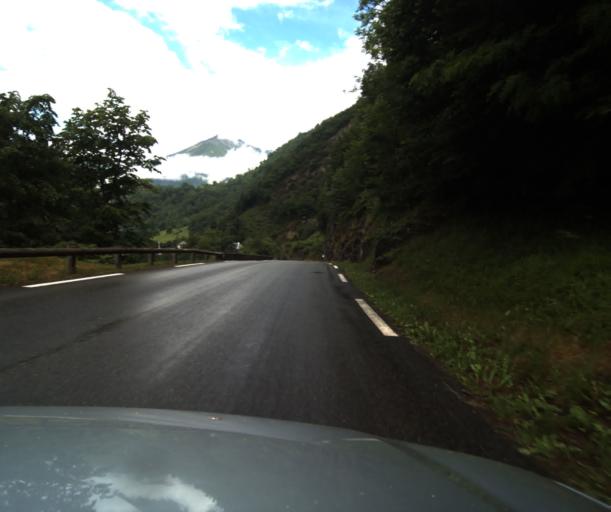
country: FR
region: Midi-Pyrenees
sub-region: Departement des Hautes-Pyrenees
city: Luz-Saint-Sauveur
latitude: 42.8549
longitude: -0.0057
